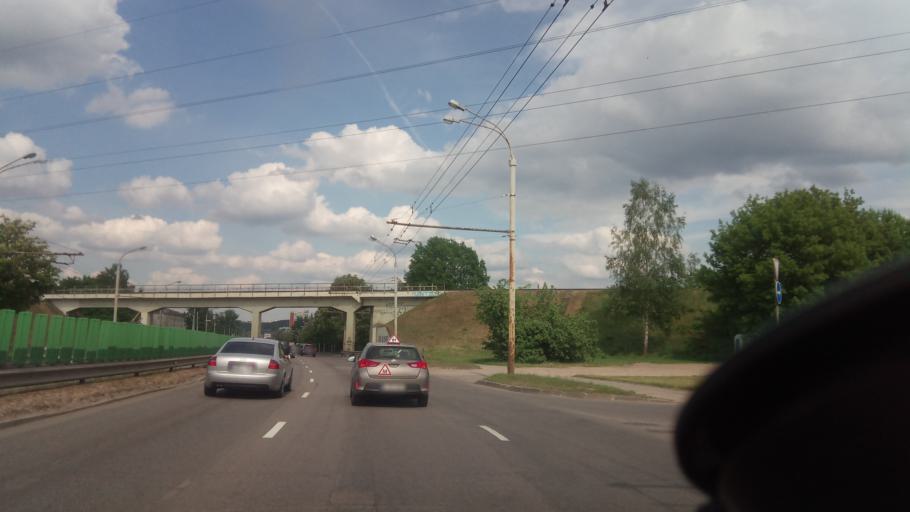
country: LT
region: Vilnius County
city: Lazdynai
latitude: 54.6454
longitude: 25.2030
